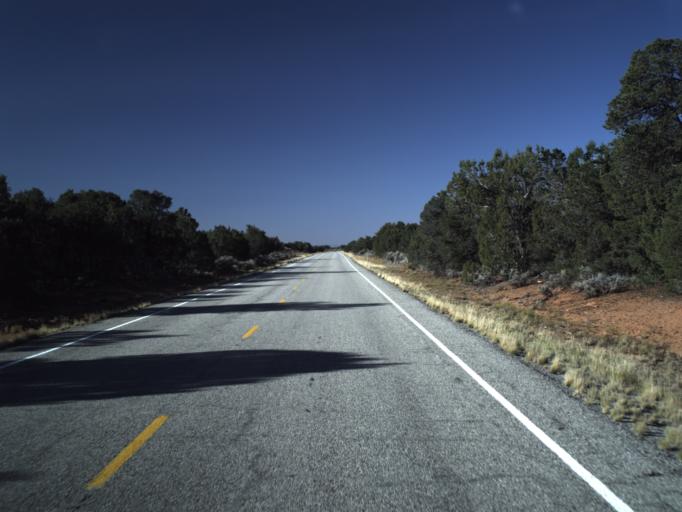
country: US
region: Utah
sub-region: San Juan County
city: Blanding
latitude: 37.5534
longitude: -109.9369
